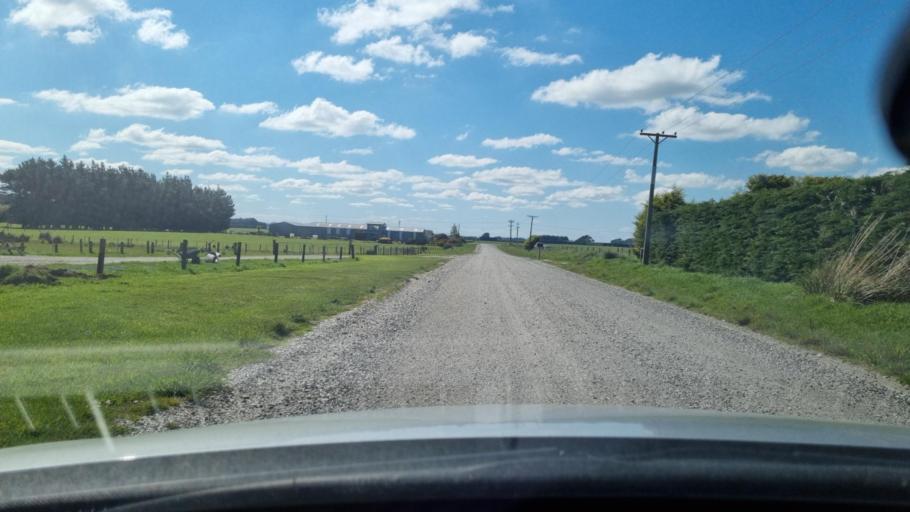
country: NZ
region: Southland
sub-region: Invercargill City
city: Invercargill
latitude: -46.3721
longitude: 168.2985
